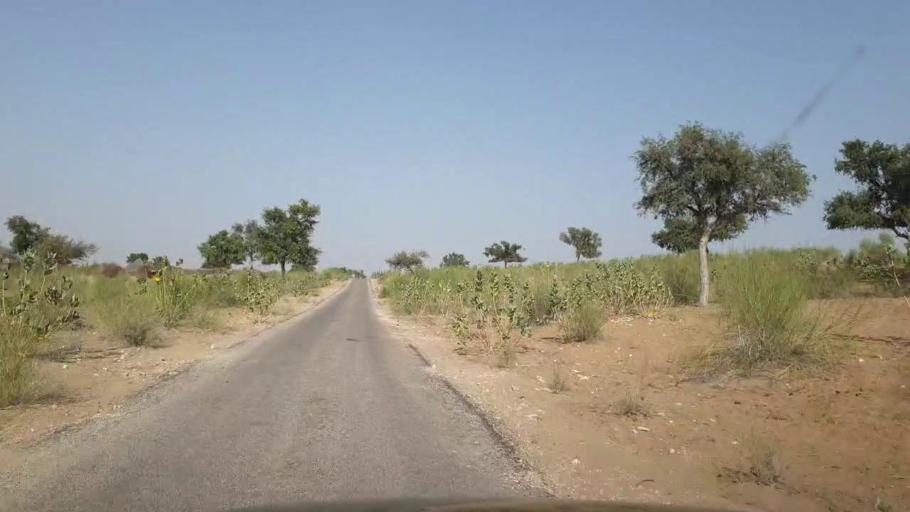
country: PK
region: Sindh
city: Islamkot
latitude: 25.1113
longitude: 70.4268
